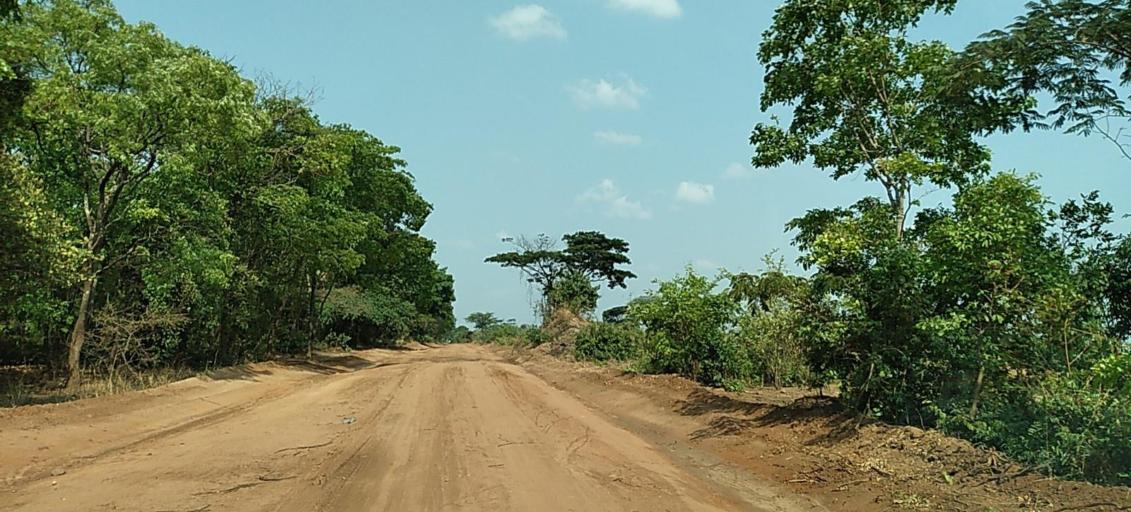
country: ZM
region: Copperbelt
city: Luanshya
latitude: -13.0906
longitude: 28.2803
